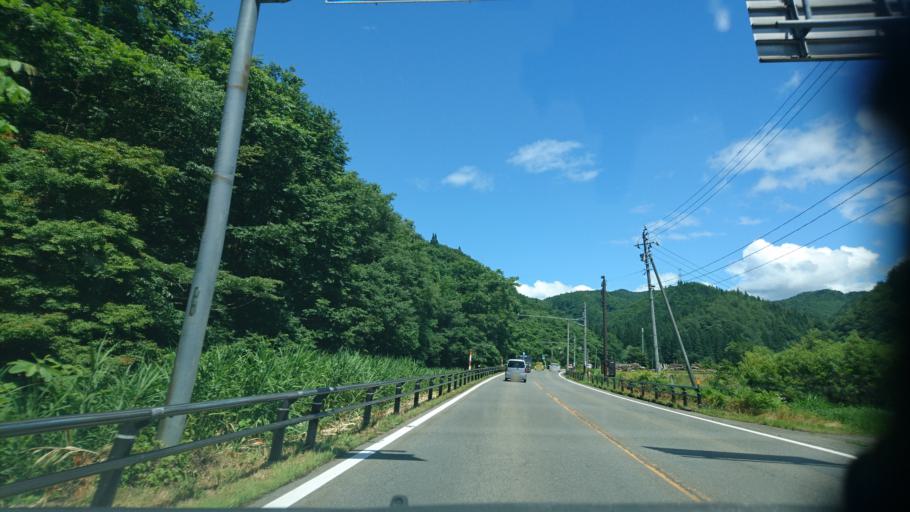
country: JP
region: Akita
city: Kakunodatemachi
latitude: 39.6566
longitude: 140.6721
